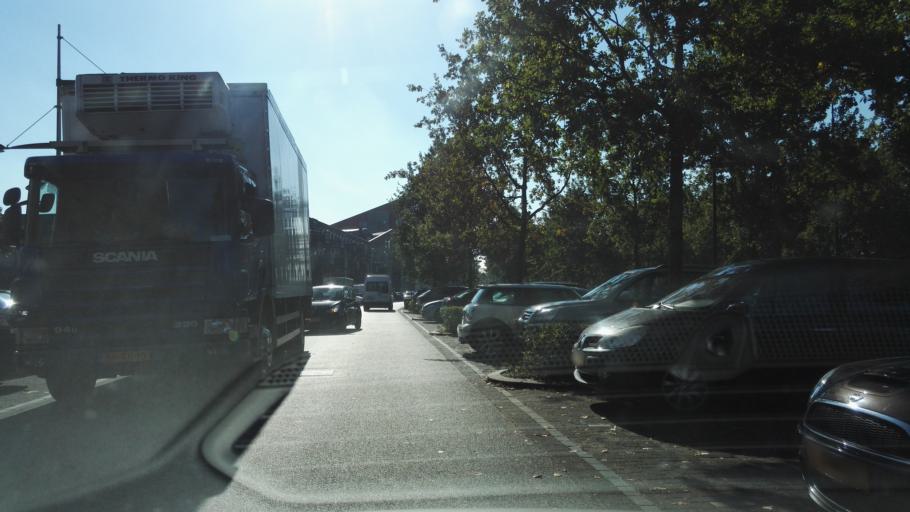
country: NL
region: Gelderland
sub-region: Gemeente Apeldoorn
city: Apeldoorn
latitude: 52.2173
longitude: 6.0026
